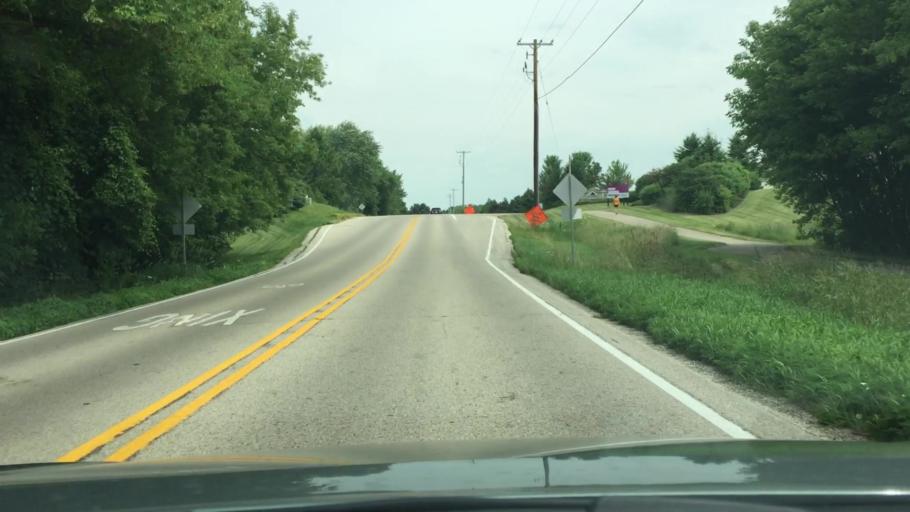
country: US
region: Wisconsin
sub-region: Waukesha County
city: Merton
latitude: 43.1355
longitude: -88.3075
